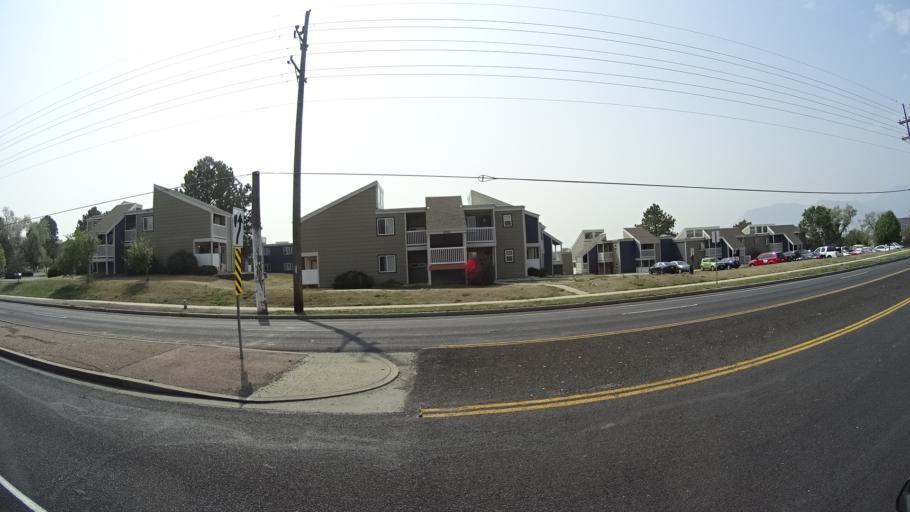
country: US
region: Colorado
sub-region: El Paso County
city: Stratmoor
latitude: 38.8255
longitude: -104.7515
